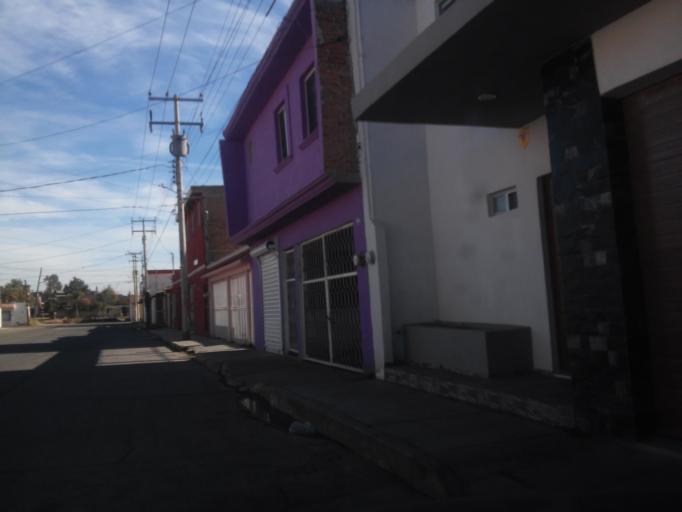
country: MX
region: Durango
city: Victoria de Durango
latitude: 24.0425
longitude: -104.6527
